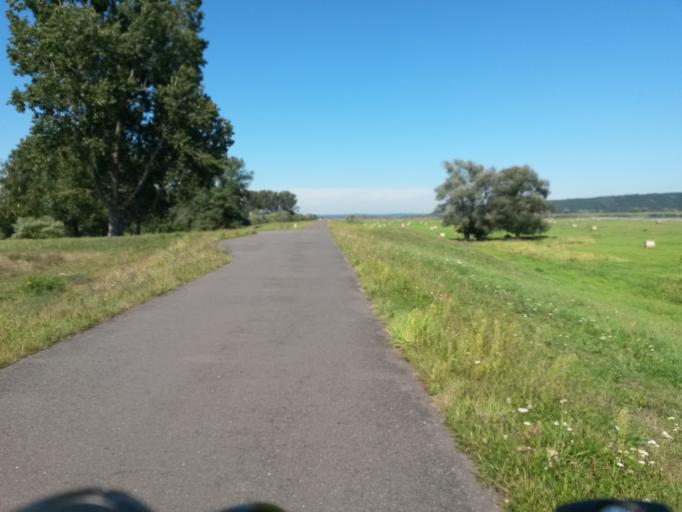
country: PL
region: West Pomeranian Voivodeship
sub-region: Powiat gryfinski
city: Cedynia
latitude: 52.9049
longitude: 14.1476
